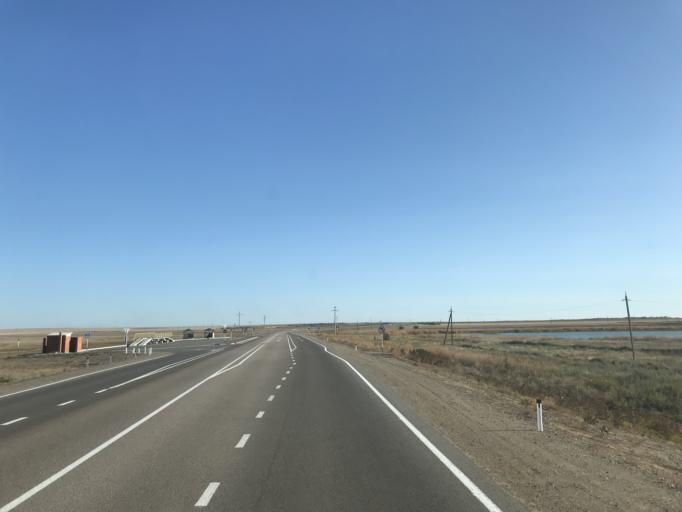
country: KZ
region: Pavlodar
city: Koktobe
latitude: 51.8835
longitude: 77.4169
